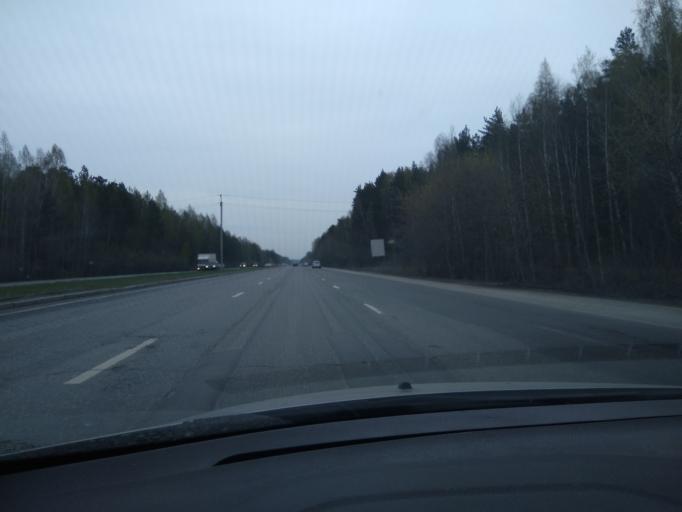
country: RU
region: Sverdlovsk
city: Istok
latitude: 56.8135
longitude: 60.7469
